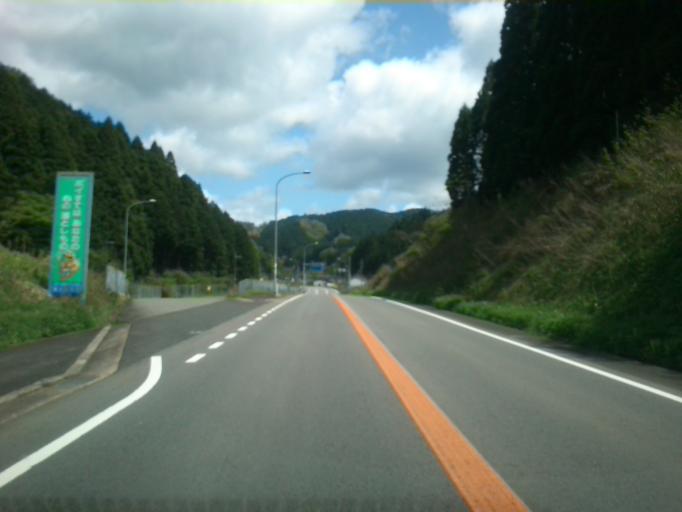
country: JP
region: Kyoto
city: Fukuchiyama
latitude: 35.4199
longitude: 135.0313
